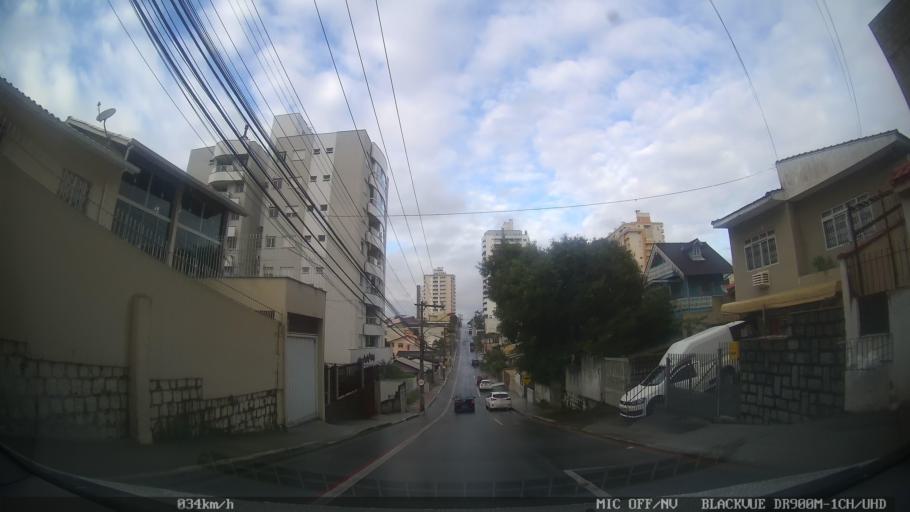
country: BR
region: Santa Catarina
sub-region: Sao Jose
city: Campinas
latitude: -27.5762
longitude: -48.6062
